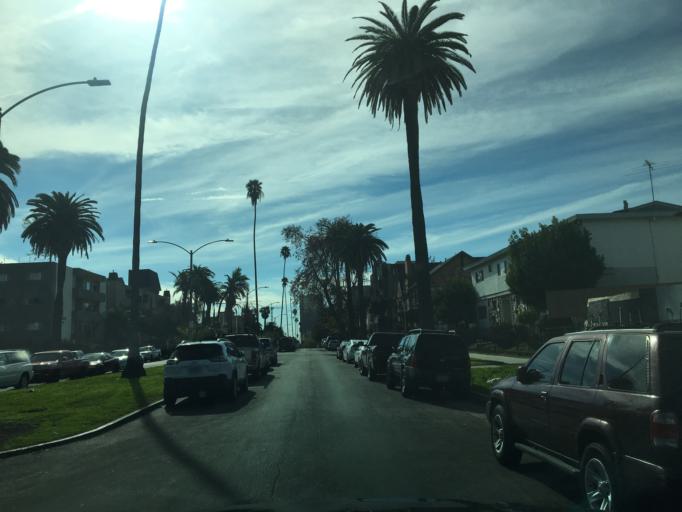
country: US
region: California
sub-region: Los Angeles County
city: Silver Lake
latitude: 34.0698
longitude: -118.2809
